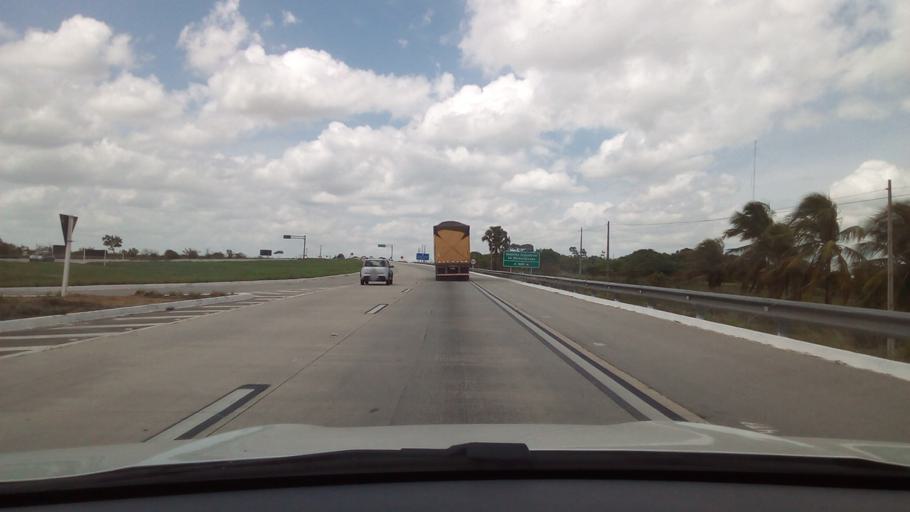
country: BR
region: Paraiba
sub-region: Mamanguape
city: Mamanguape
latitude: -6.8154
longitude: -35.1388
